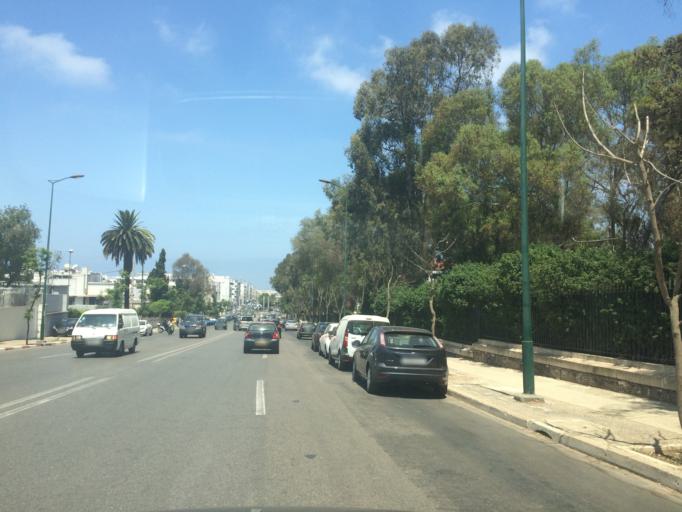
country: MA
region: Rabat-Sale-Zemmour-Zaer
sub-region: Rabat
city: Rabat
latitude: 33.9965
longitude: -6.8427
